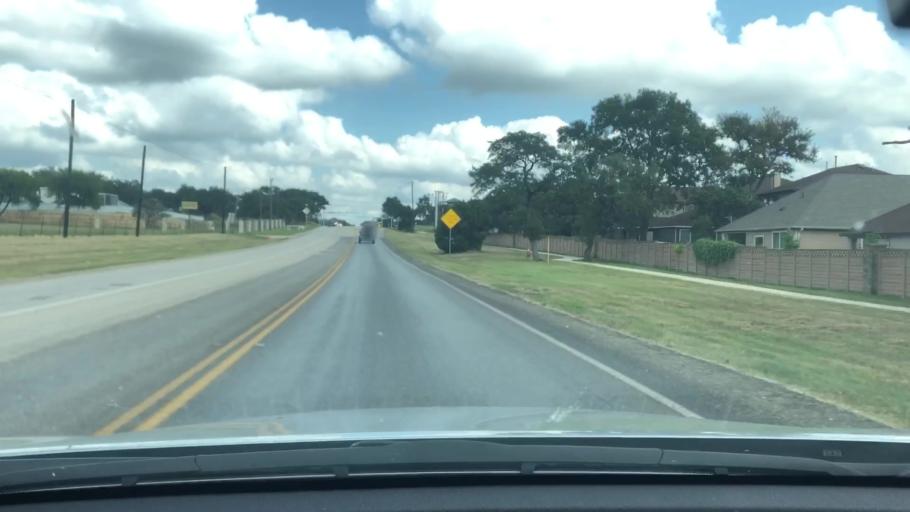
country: US
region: Texas
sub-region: Kendall County
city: Boerne
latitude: 29.7872
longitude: -98.6969
